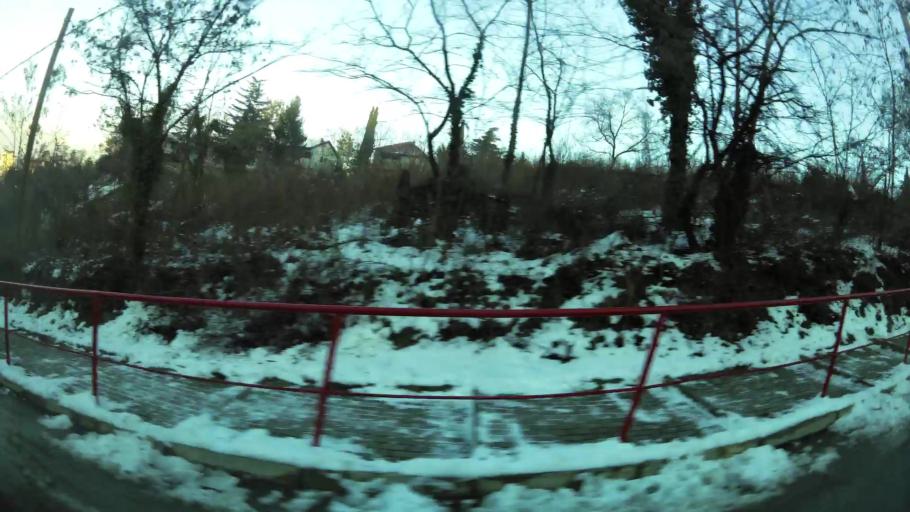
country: MK
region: Karpos
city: Skopje
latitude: 41.9906
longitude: 21.4060
